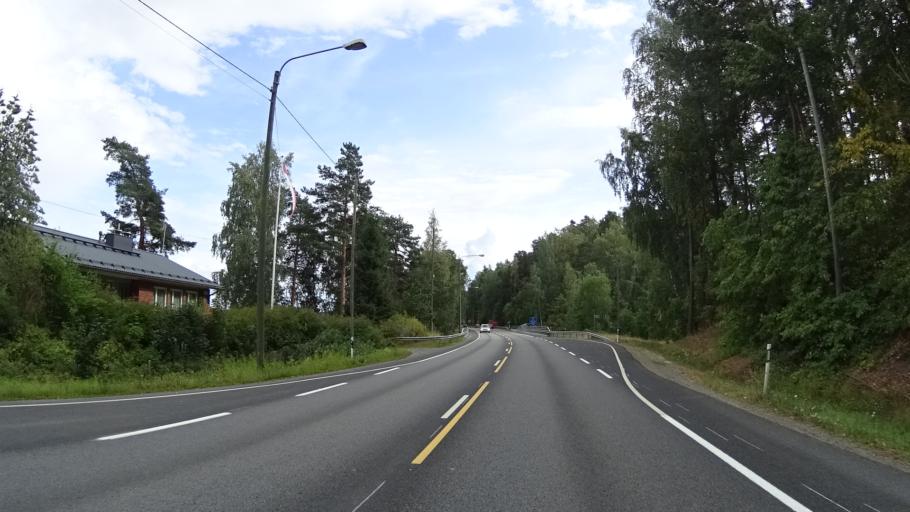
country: FI
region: Pirkanmaa
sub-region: Tampere
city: Kangasala
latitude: 61.4213
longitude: 24.1409
